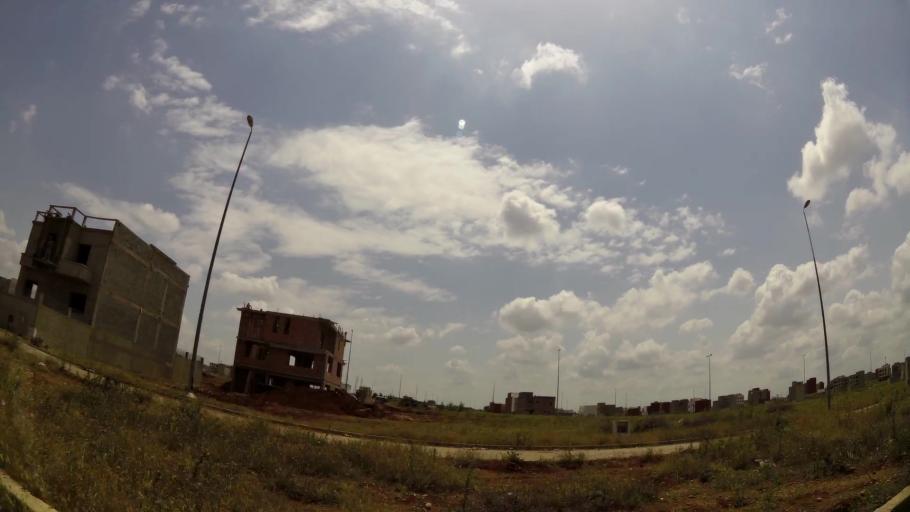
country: MA
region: Rabat-Sale-Zemmour-Zaer
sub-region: Khemisset
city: Tiflet
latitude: 34.0035
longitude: -6.5399
